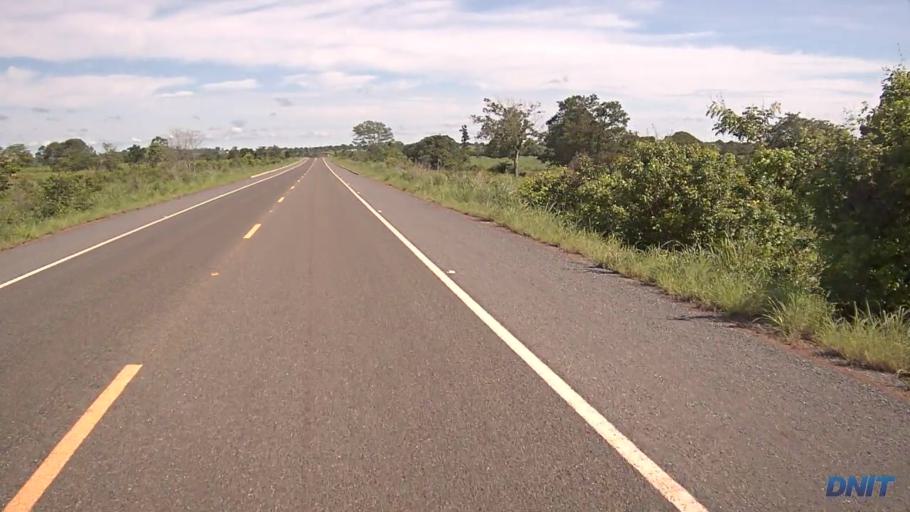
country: BR
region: Goias
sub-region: Sao Miguel Do Araguaia
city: Sao Miguel do Araguaia
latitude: -13.3084
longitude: -50.1724
